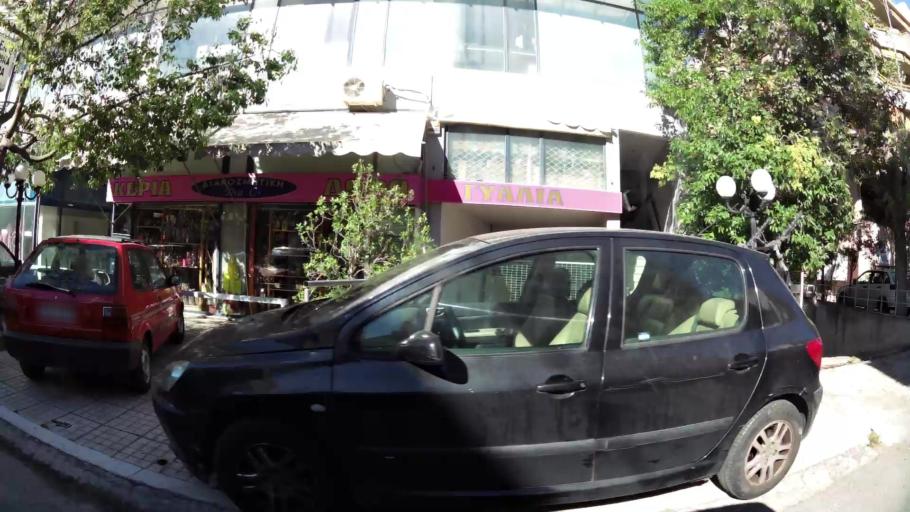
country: GR
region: Attica
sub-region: Nomarchia Athinas
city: Khalandrion
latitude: 38.0240
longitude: 23.8062
